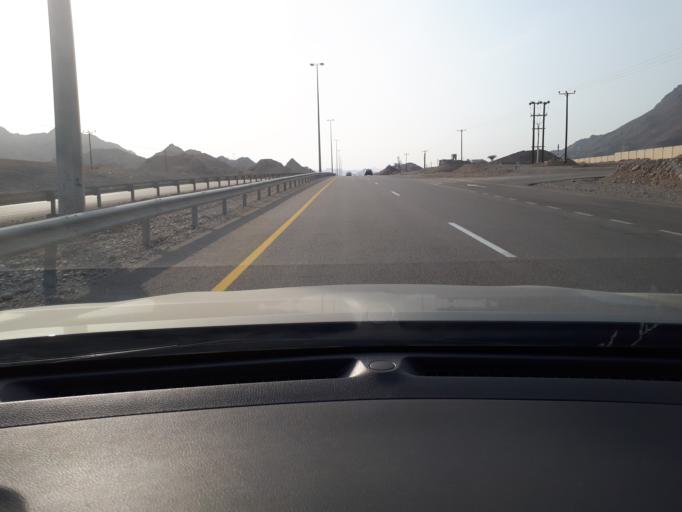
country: OM
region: Muhafazat Masqat
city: Muscat
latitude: 23.2585
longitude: 58.7720
